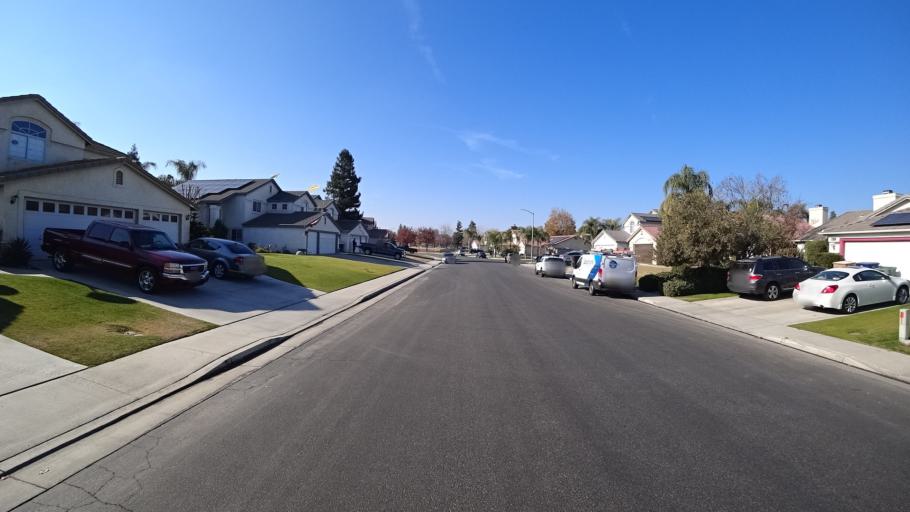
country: US
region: California
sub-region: Kern County
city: Greenacres
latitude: 35.3192
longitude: -119.1119
